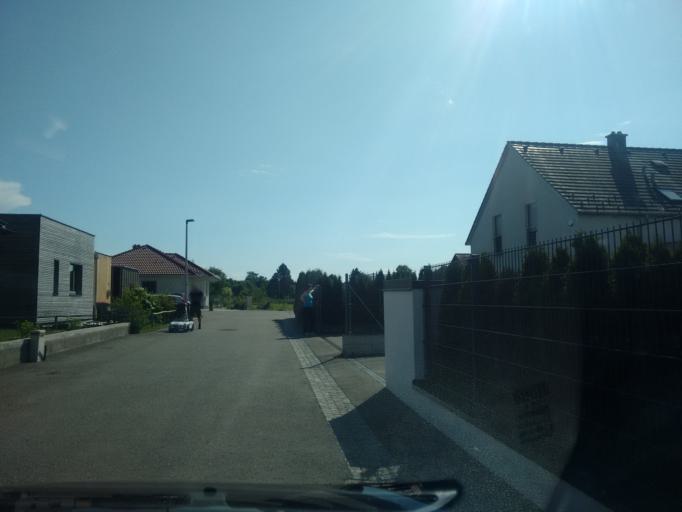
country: AT
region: Upper Austria
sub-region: Wels-Land
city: Gunskirchen
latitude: 48.1280
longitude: 13.9379
